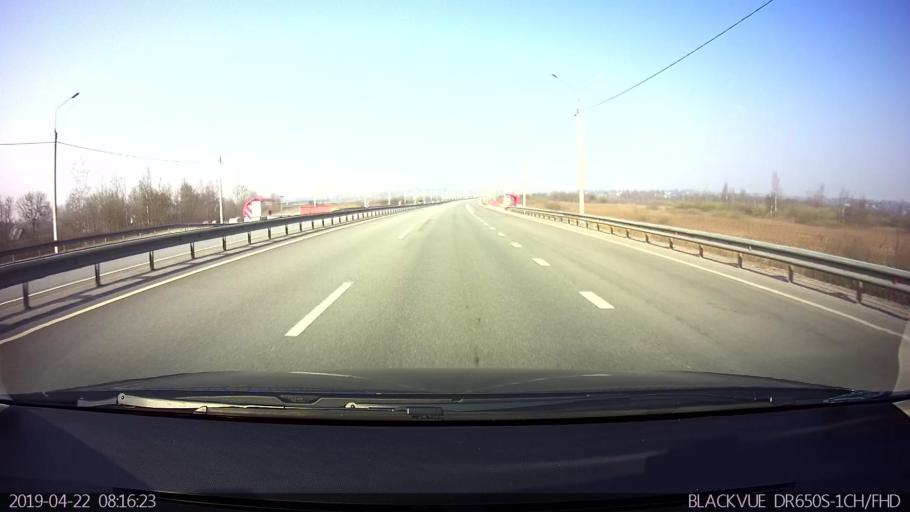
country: RU
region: Smolensk
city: Yartsevo
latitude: 55.0792
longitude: 32.6952
